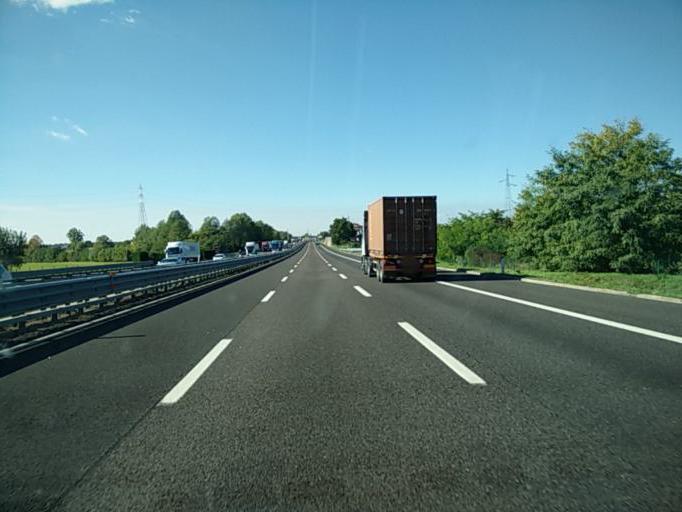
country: IT
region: Veneto
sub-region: Provincia di Verona
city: Castelnuovo del Garda
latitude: 45.4278
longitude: 10.7462
